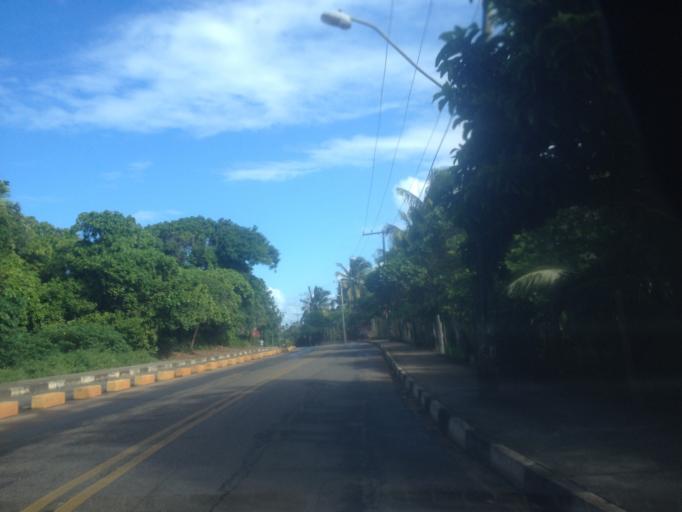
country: BR
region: Bahia
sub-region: Mata De Sao Joao
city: Mata de Sao Joao
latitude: -12.6028
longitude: -38.0406
